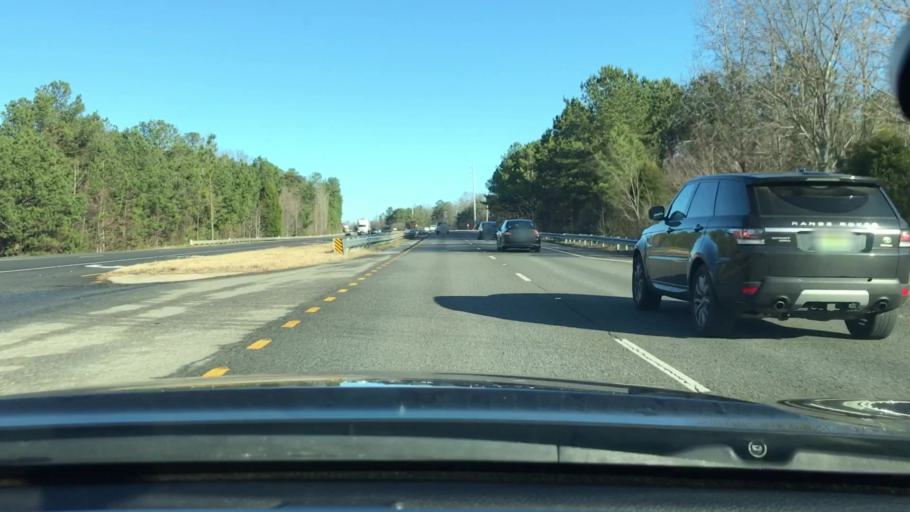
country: US
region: Alabama
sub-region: Shelby County
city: Meadowbrook
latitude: 33.3773
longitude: -86.6666
